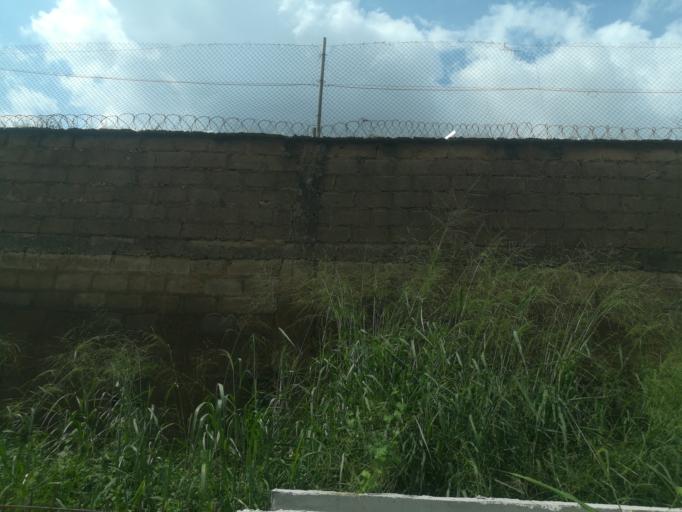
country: NG
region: Oyo
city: Ibadan
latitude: 7.3550
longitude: 3.8455
